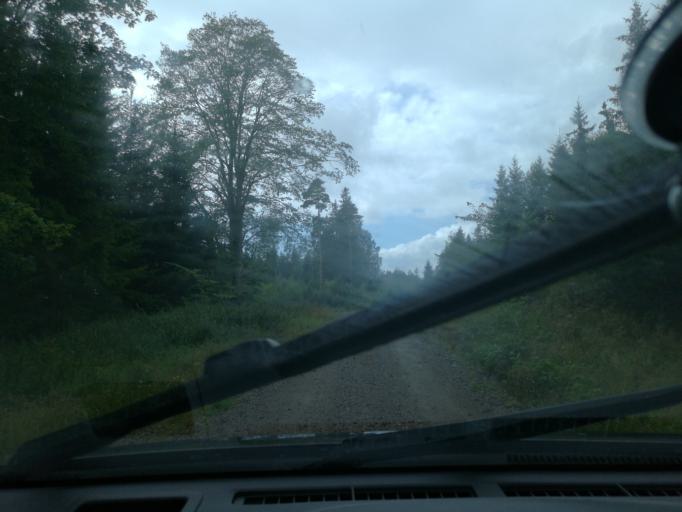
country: SE
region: Kronoberg
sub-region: Alvesta Kommun
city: Vislanda
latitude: 56.7052
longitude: 14.4101
